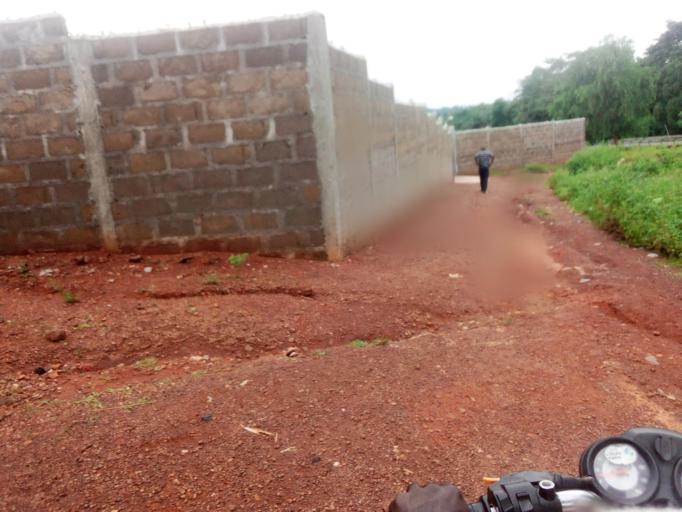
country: SL
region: Northern Province
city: Kambia
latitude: 9.1152
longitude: -12.9296
